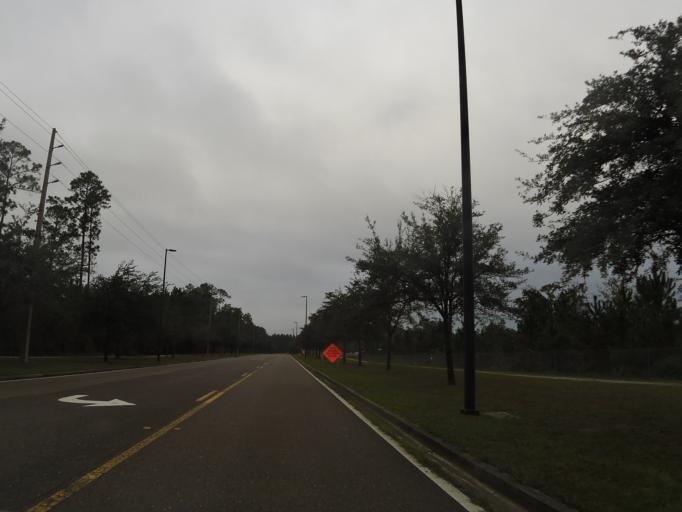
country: US
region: Florida
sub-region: Duval County
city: Baldwin
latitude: 30.2409
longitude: -81.8832
